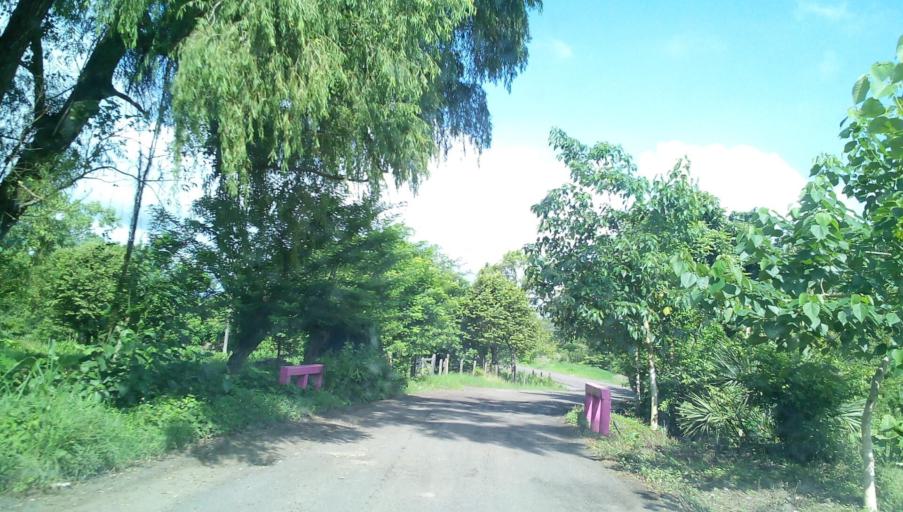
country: MX
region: Veracruz
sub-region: Citlaltepetl
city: Las Sabinas
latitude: 21.3428
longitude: -97.8875
